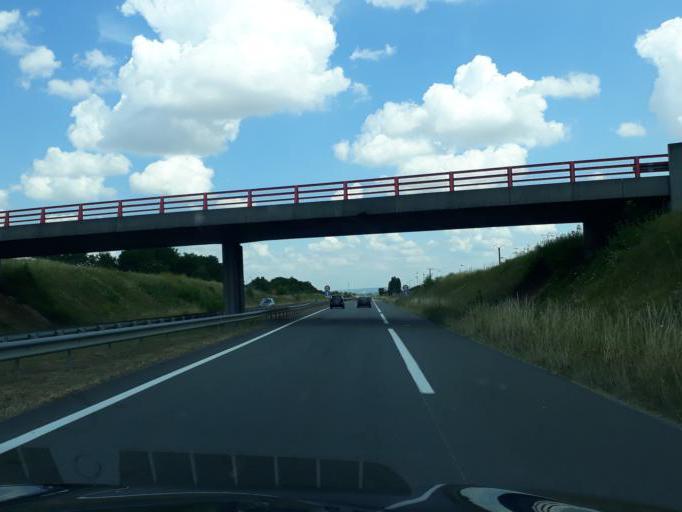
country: FR
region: Centre
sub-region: Departement du Cher
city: Bourges
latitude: 47.0665
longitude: 2.4332
